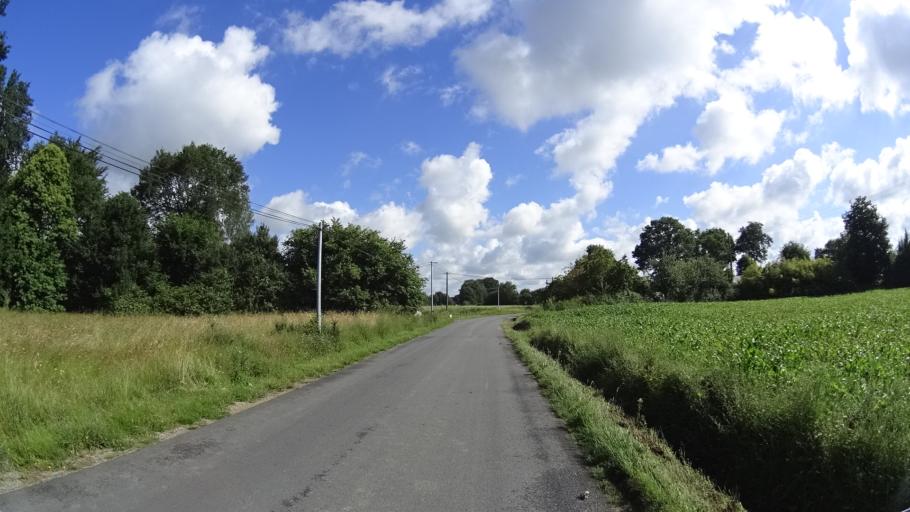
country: FR
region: Brittany
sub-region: Departement d'Ille-et-Vilaine
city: Saint-Gilles
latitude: 48.1314
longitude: -1.8167
